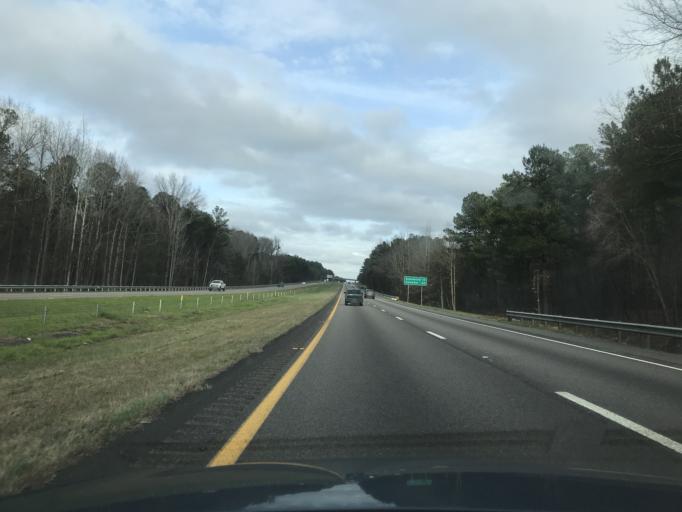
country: US
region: South Carolina
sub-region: Edgefield County
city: Murphys Estates
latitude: 33.5724
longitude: -81.9112
